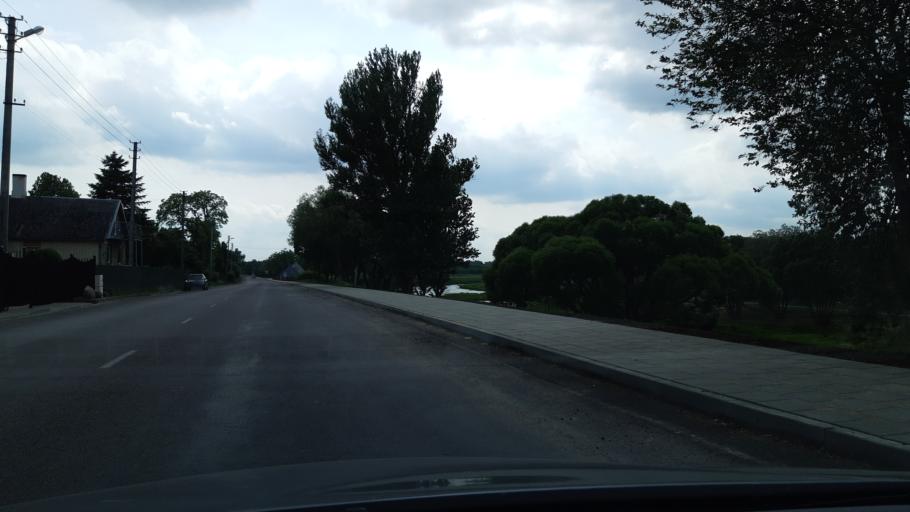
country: LT
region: Kauno apskritis
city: Kedainiai
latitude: 55.2836
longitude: 23.9830
